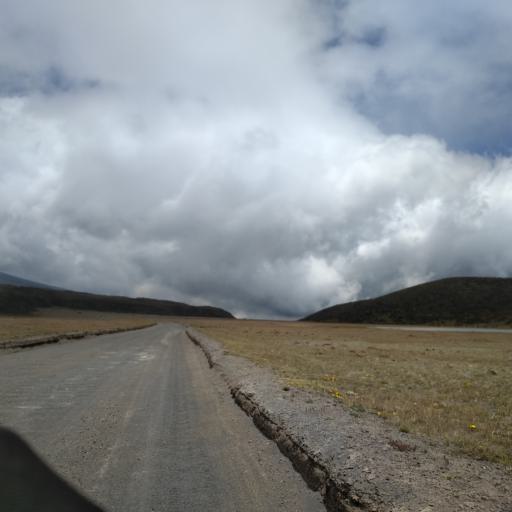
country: EC
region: Pichincha
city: Machachi
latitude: -0.6179
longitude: -78.4739
